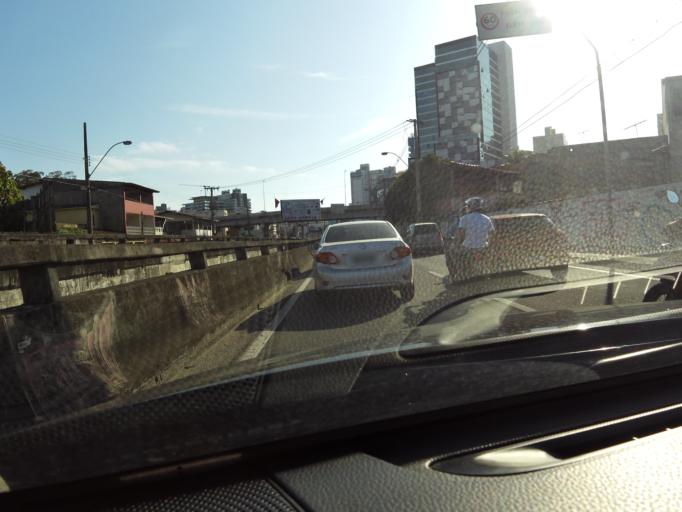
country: BR
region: Espirito Santo
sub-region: Vila Velha
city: Vila Velha
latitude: -20.3419
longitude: -40.2911
